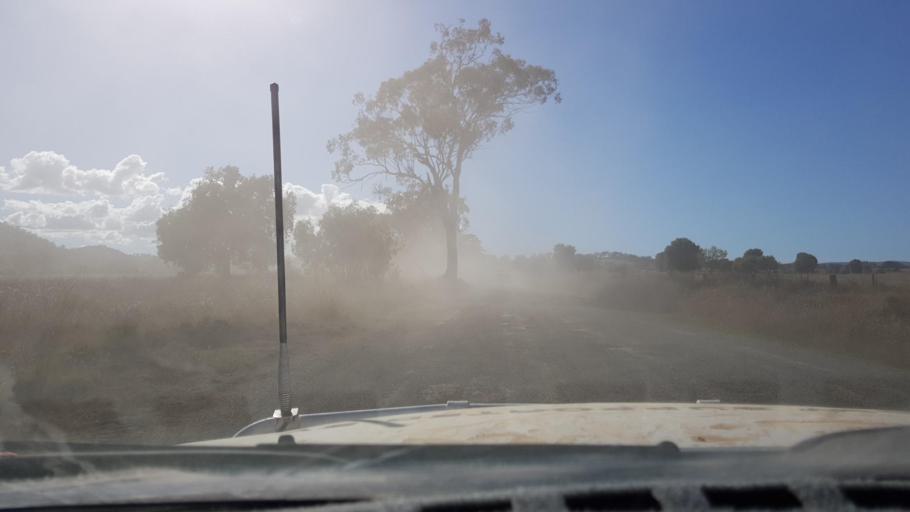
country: AU
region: New South Wales
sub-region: Narrabri
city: Blair Athol
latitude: -30.6697
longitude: 150.4567
